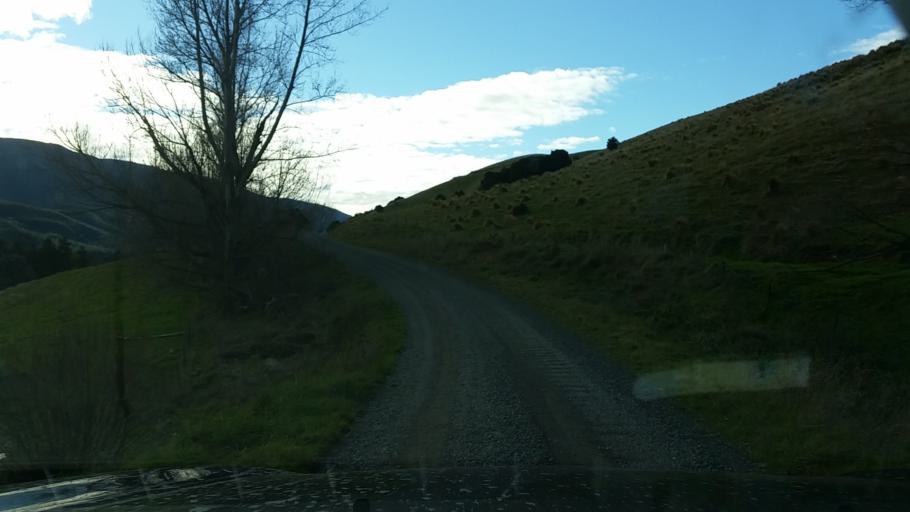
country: NZ
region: Marlborough
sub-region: Marlborough District
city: Blenheim
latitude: -41.7707
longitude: 173.8574
